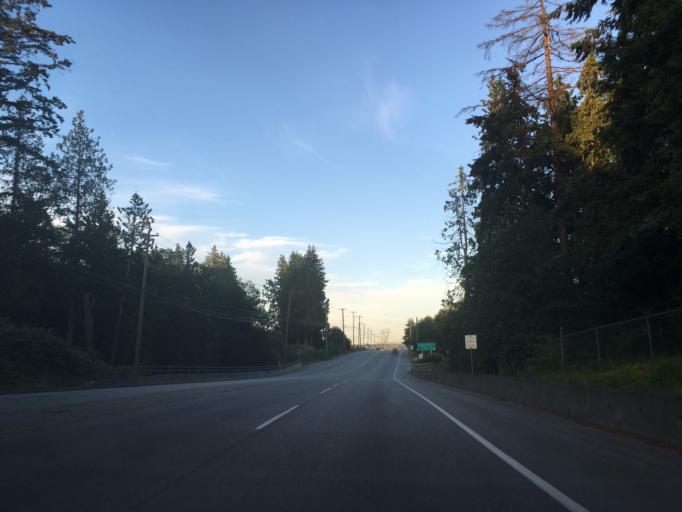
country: US
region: Washington
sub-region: Whatcom County
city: Blaine
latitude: 49.0165
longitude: -122.7541
